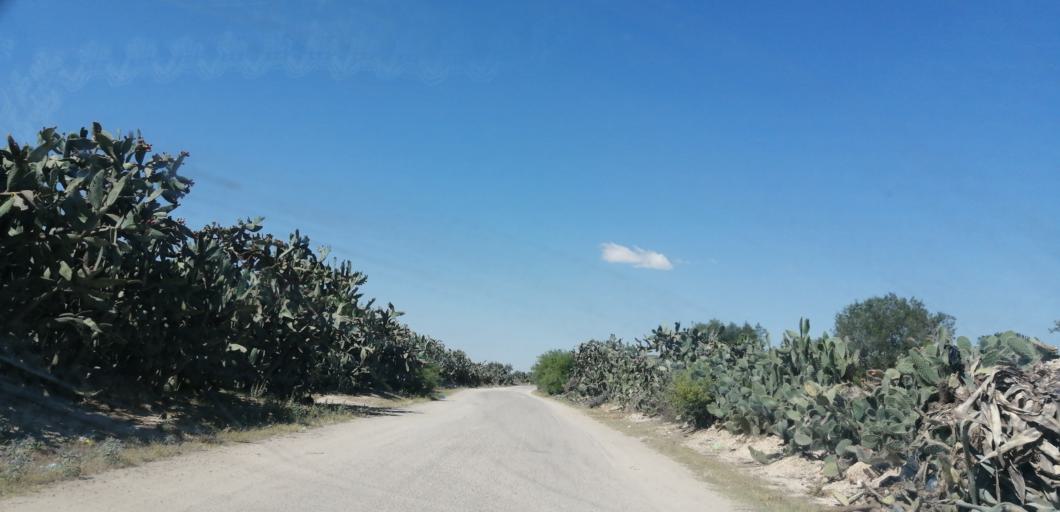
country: TN
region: Al Qayrawan
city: Kairouan
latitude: 35.6308
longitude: 9.9408
